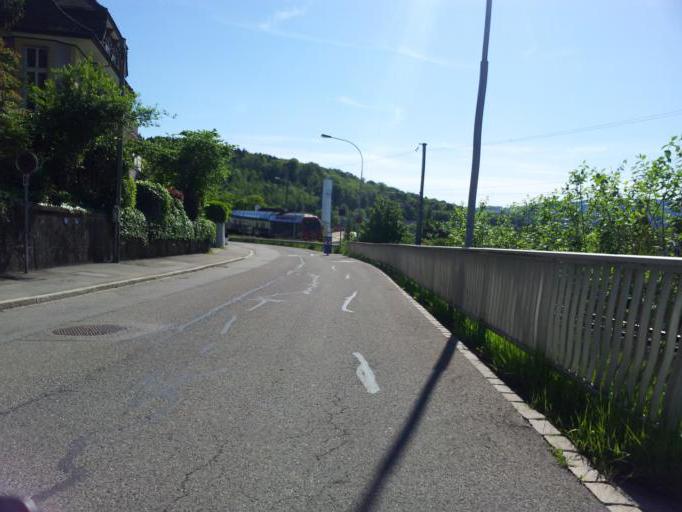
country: CH
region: Zurich
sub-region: Bezirk Dietikon
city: Schlieren
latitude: 47.3949
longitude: 8.4512
